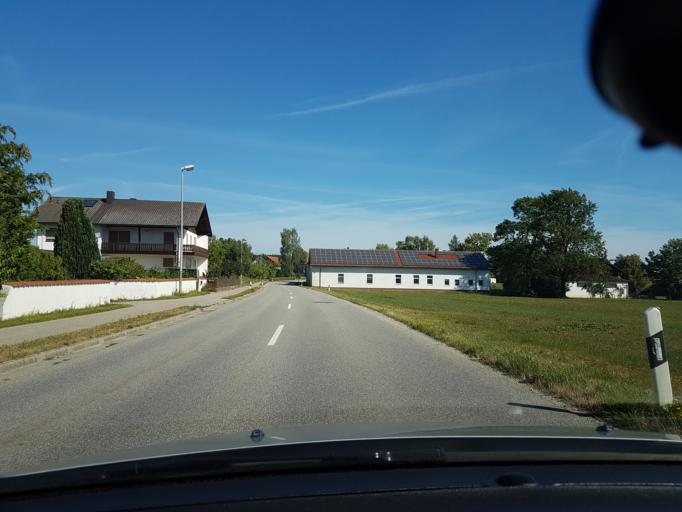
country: DE
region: Bavaria
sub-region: Lower Bavaria
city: Furth
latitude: 48.3975
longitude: 12.3932
